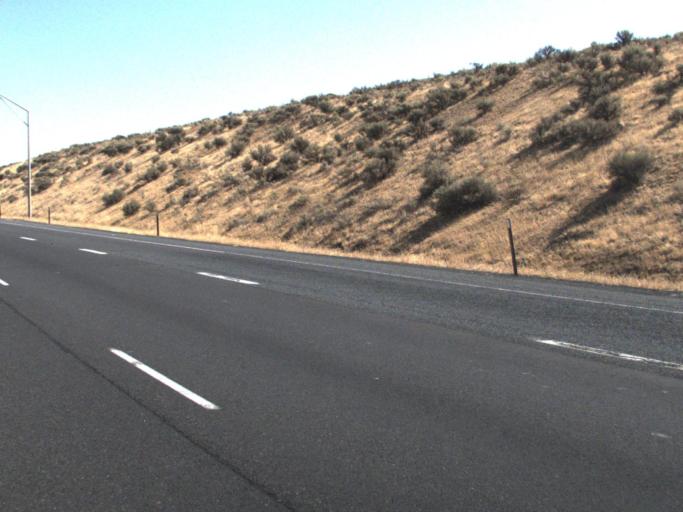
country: US
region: Washington
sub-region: Grant County
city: Warden
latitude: 47.0868
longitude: -118.8673
